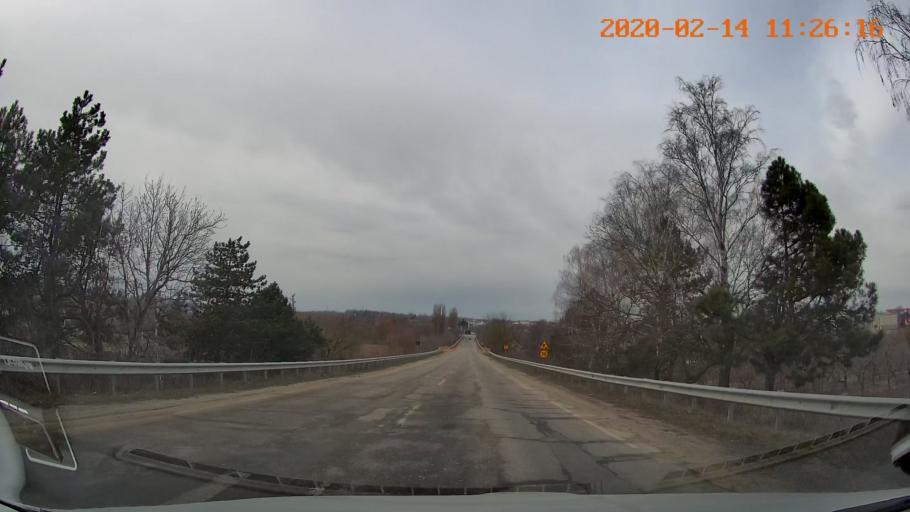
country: MD
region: Briceni
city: Briceni
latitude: 48.3516
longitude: 27.0920
